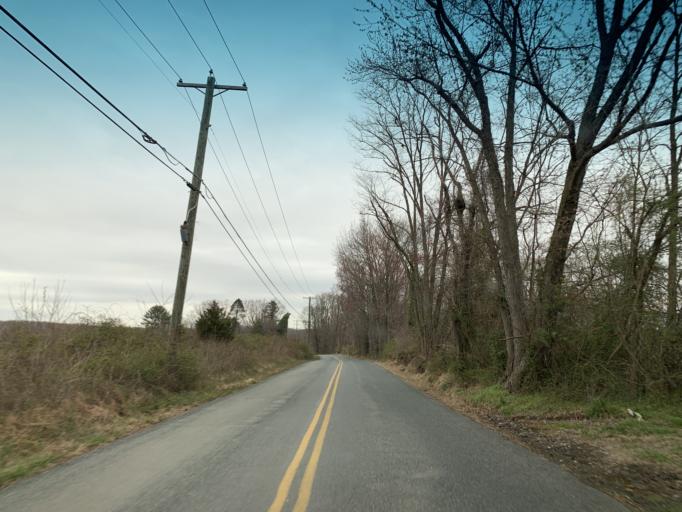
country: US
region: Maryland
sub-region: Harford County
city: Aberdeen
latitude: 39.5359
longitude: -76.2033
